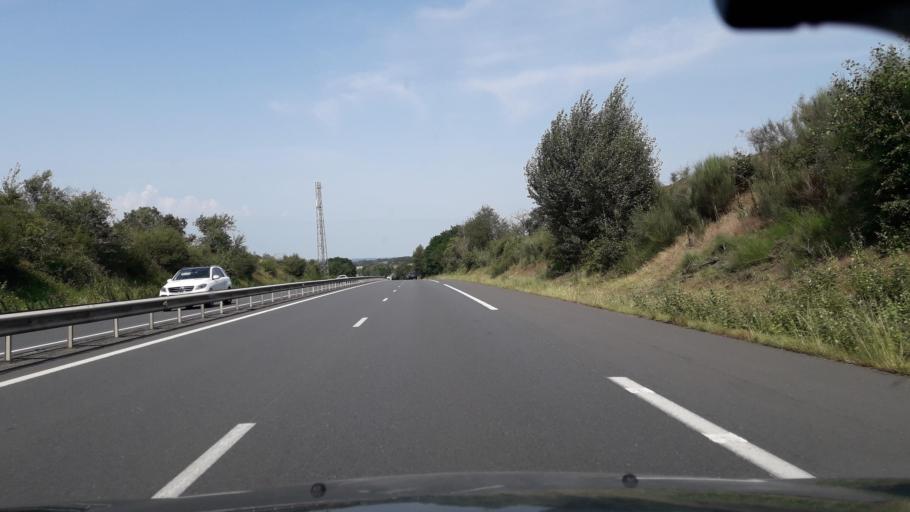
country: FR
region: Auvergne
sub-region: Departement de l'Allier
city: Montmarault
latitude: 46.3410
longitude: 2.8805
